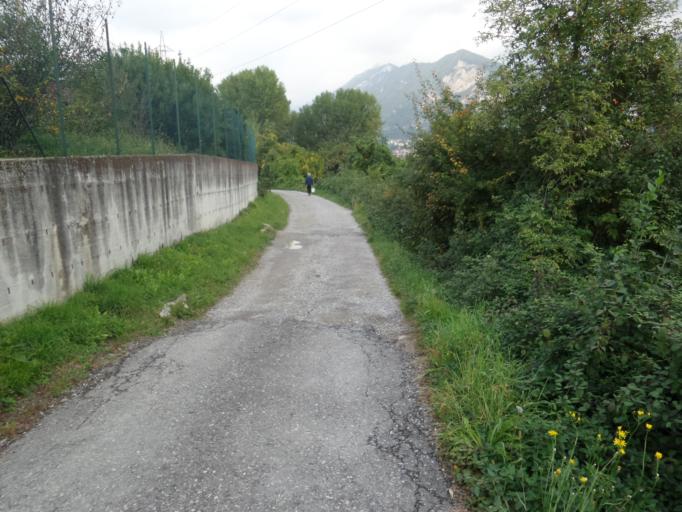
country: IT
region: Lombardy
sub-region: Provincia di Lecco
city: Olginate
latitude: 45.7882
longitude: 9.4125
